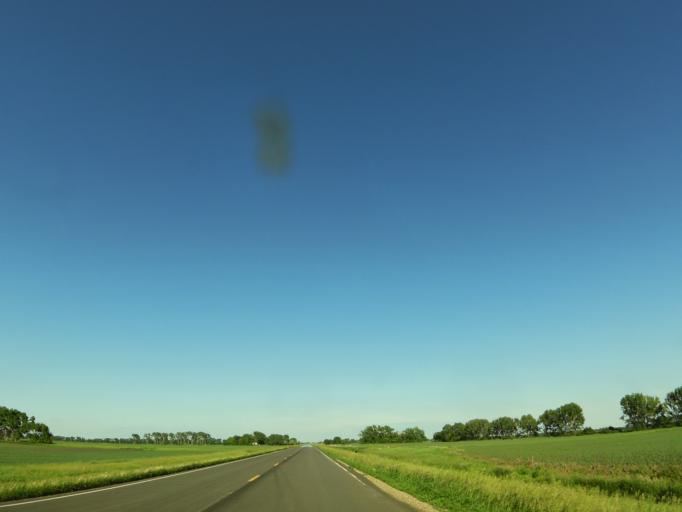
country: US
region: North Dakota
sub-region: Grand Forks County
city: Grand Forks Air Force Base
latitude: 48.1357
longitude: -97.2259
